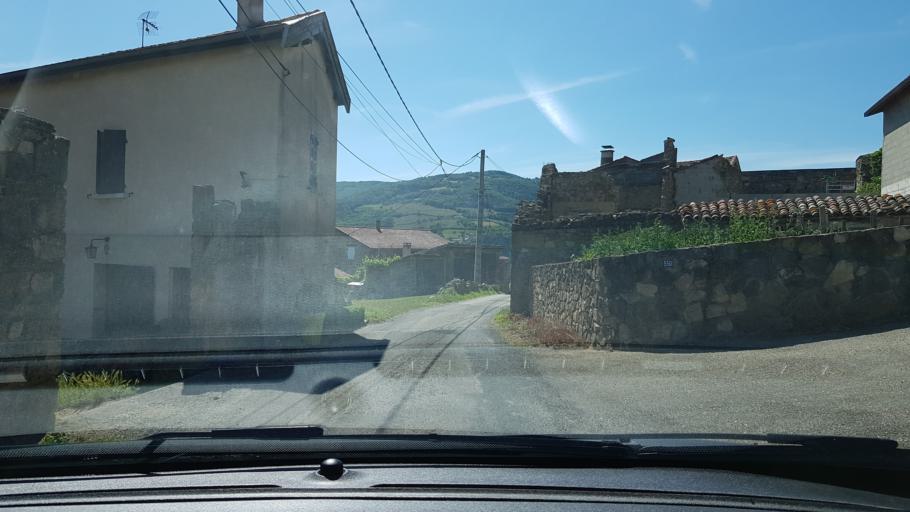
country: FR
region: Rhone-Alpes
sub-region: Departement du Rhone
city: Saint-Didier-sous-Riverie
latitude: 45.5861
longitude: 4.6134
